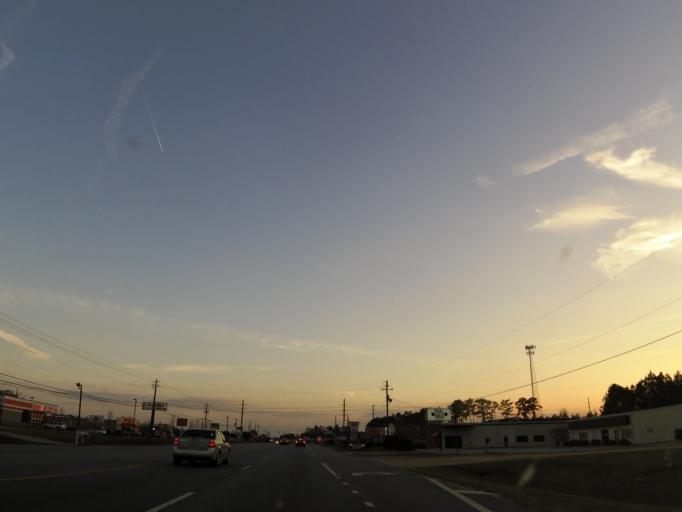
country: US
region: Georgia
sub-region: Dougherty County
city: Albany
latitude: 31.6368
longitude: -84.1761
